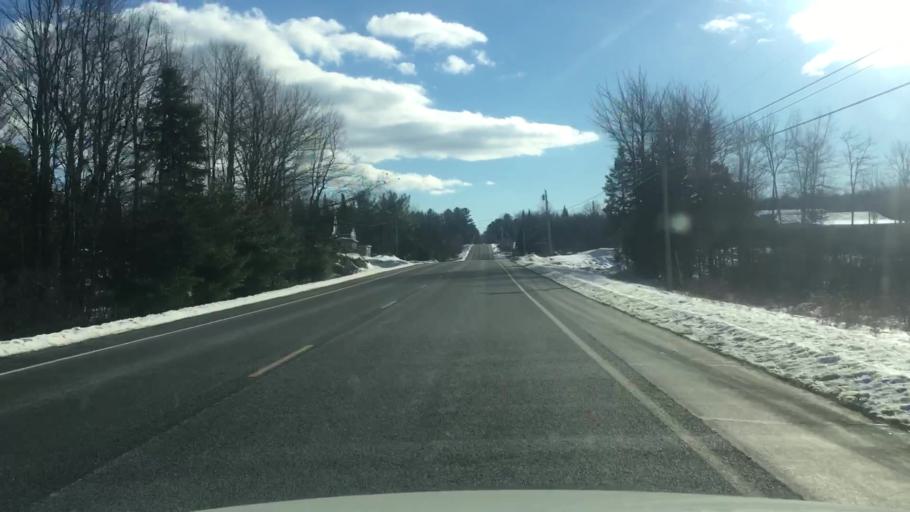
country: US
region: Maine
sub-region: Somerset County
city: Madison
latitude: 44.8450
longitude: -69.7893
